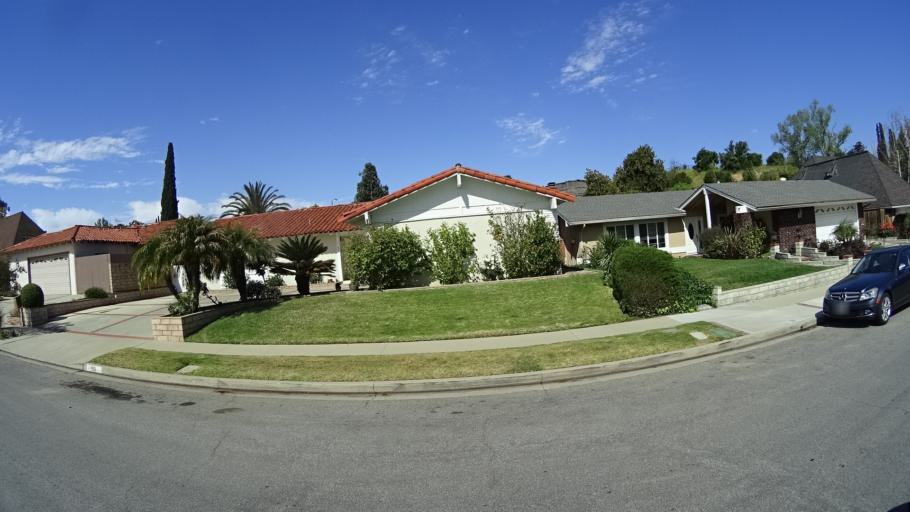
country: US
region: California
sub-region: Ventura County
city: Casa Conejo
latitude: 34.1798
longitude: -118.9246
